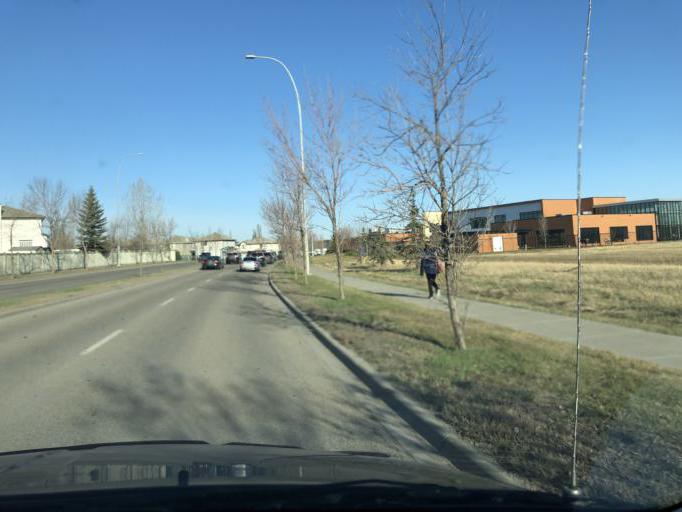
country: CA
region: Alberta
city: Calgary
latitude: 50.9565
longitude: -114.0049
